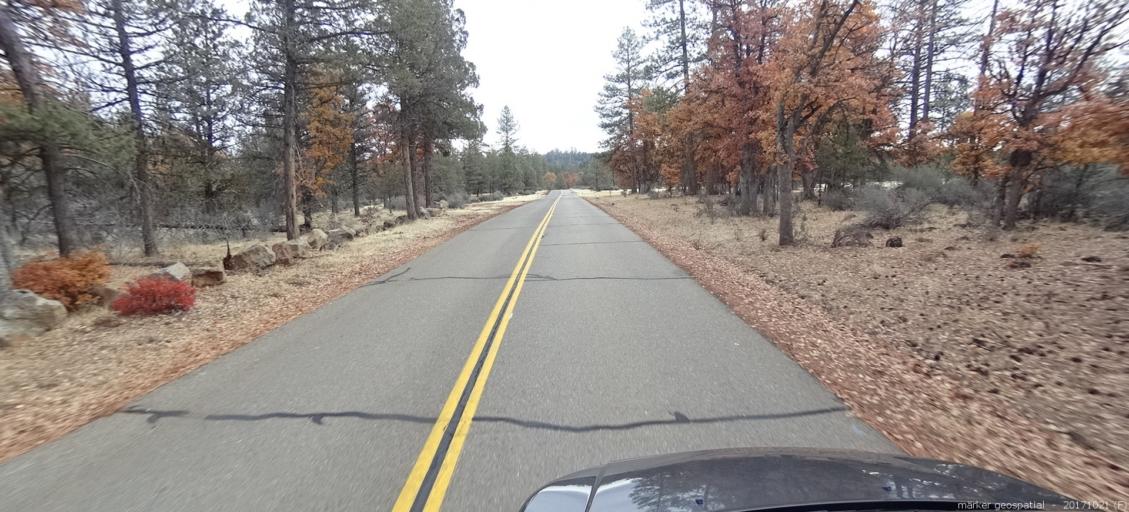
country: US
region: California
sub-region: Shasta County
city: Burney
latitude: 40.9316
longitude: -121.5541
